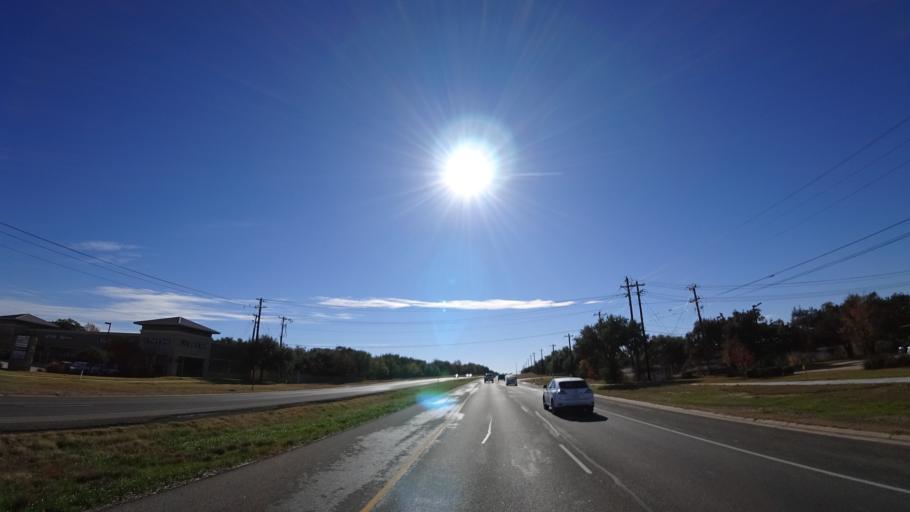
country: US
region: Texas
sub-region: Williamson County
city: Brushy Creek
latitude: 30.4966
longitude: -97.7750
